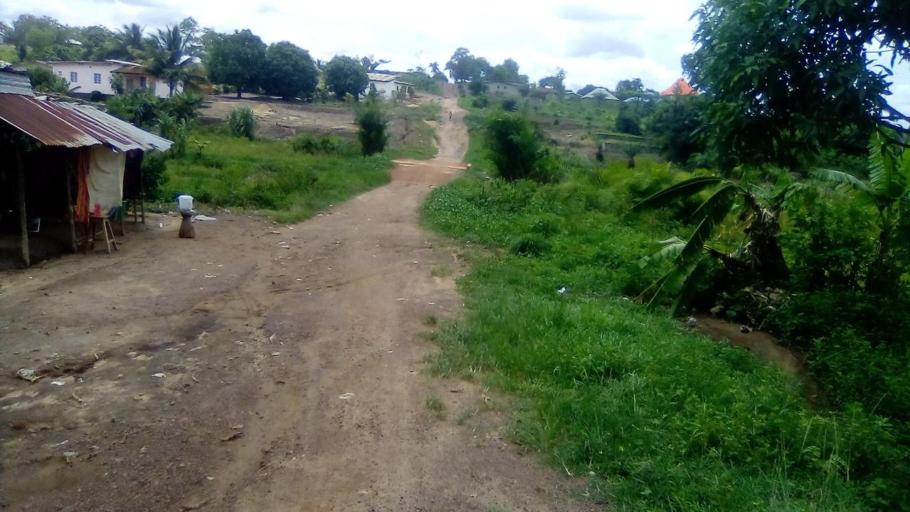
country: SL
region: Southern Province
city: Bo
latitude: 7.9341
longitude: -11.7392
